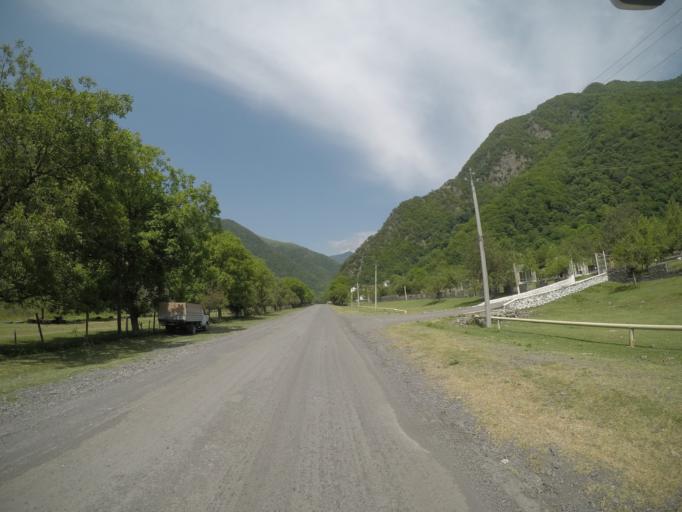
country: AZ
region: Qakh Rayon
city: Qaxbas
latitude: 41.4597
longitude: 47.0276
